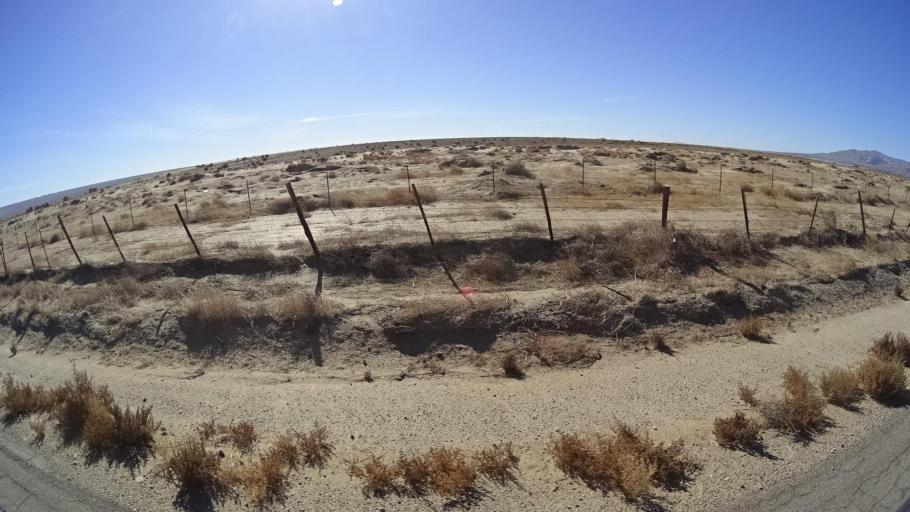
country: US
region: California
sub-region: Kern County
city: California City
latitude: 35.2868
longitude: -117.9766
